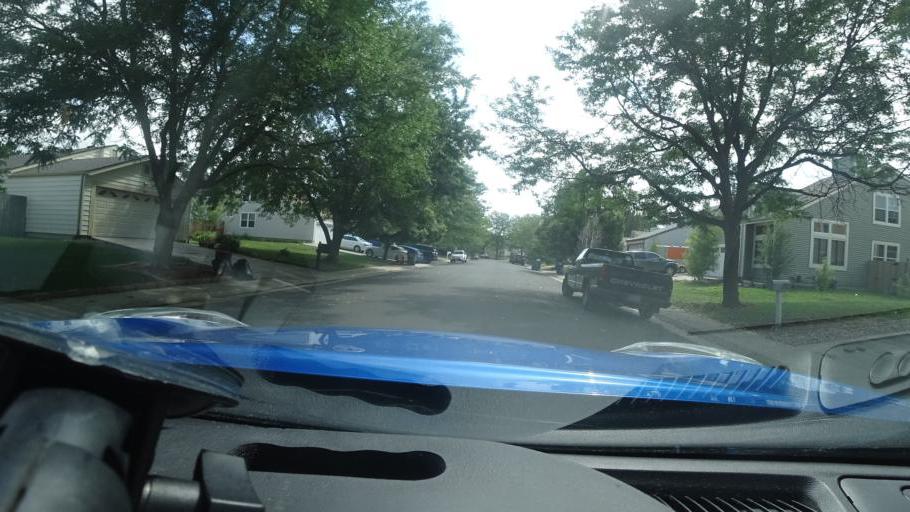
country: US
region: Colorado
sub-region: Adams County
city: Aurora
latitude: 39.7180
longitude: -104.8565
